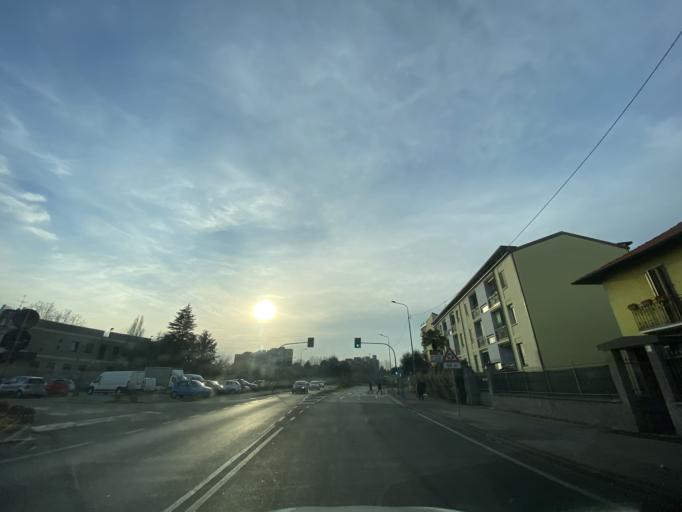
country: IT
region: Lombardy
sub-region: Citta metropolitana di Milano
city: Vimodrone
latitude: 45.5119
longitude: 9.2865
